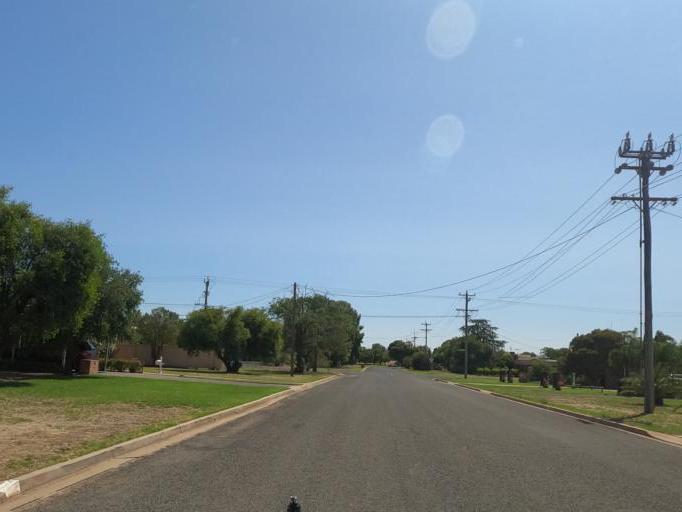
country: AU
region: New South Wales
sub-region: Corowa Shire
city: Mulwala
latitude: -35.9846
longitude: 146.0081
